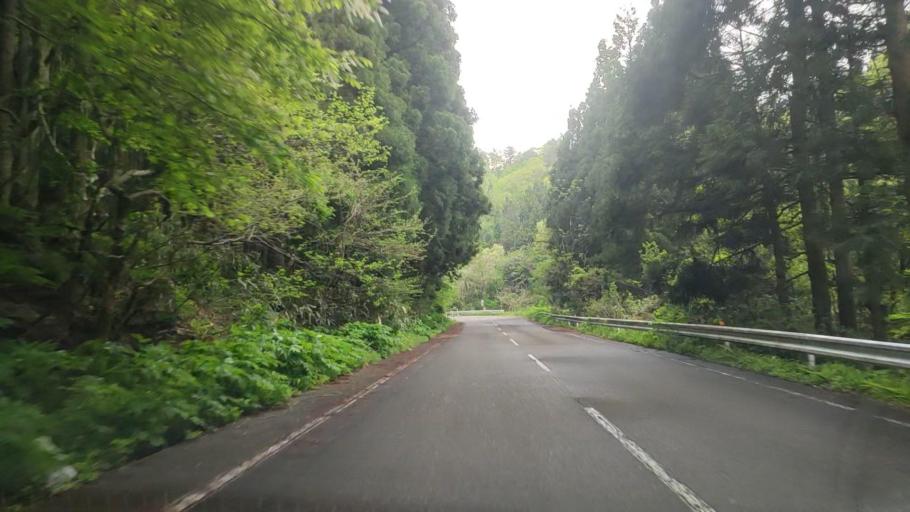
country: JP
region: Niigata
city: Gosen
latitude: 37.7104
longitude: 139.0951
